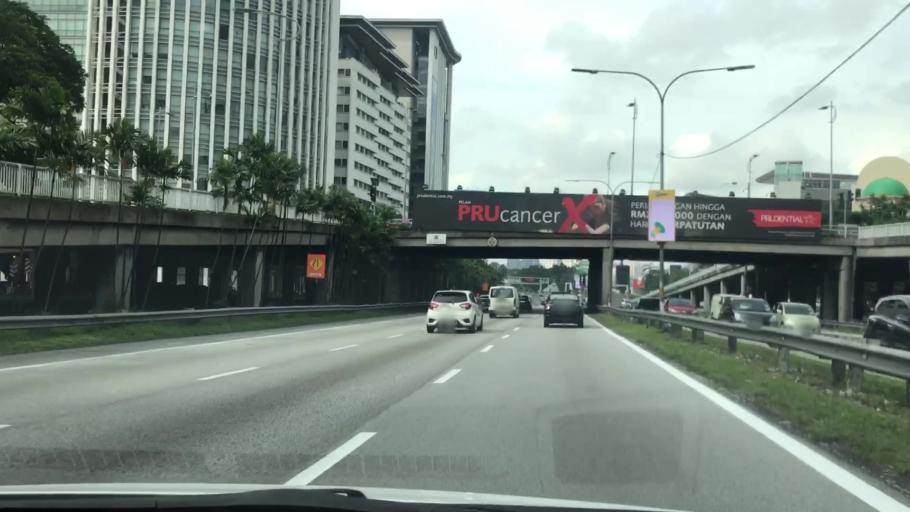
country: MY
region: Selangor
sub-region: Petaling
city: Petaling Jaya
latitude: 3.1031
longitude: 101.6405
